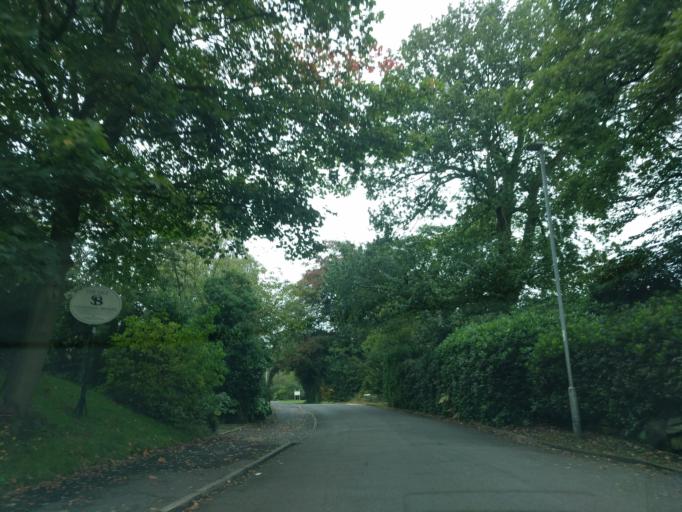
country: GB
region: England
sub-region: Staffordshire
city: Audley
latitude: 53.0086
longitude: -2.3375
